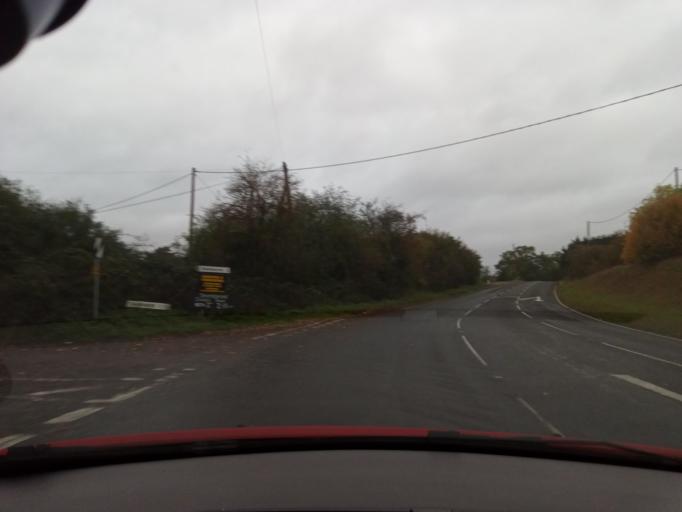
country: GB
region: England
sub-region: Essex
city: Great Yeldham
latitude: 52.0211
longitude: 0.5530
